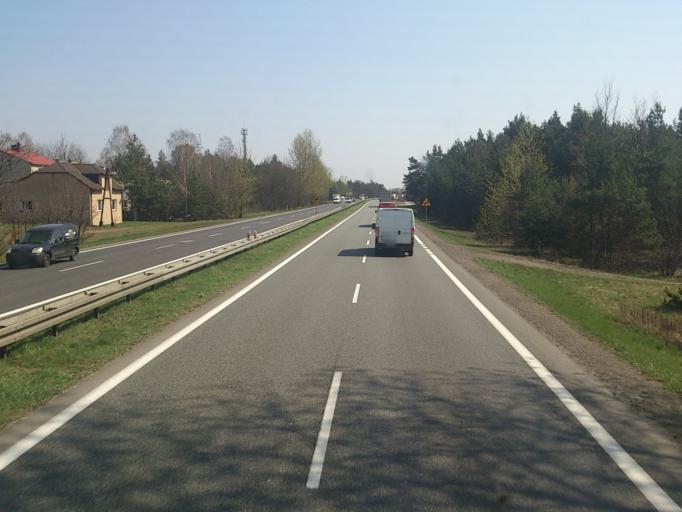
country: PL
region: Silesian Voivodeship
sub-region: Powiat bedzinski
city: Siewierz
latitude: 50.4826
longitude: 19.2212
